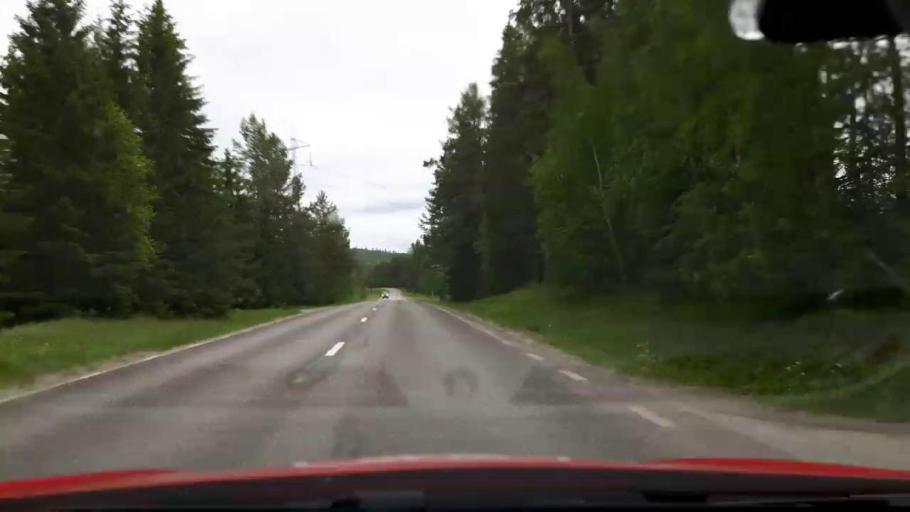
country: SE
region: Jaemtland
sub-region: Ragunda Kommun
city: Hammarstrand
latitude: 63.0683
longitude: 16.3862
